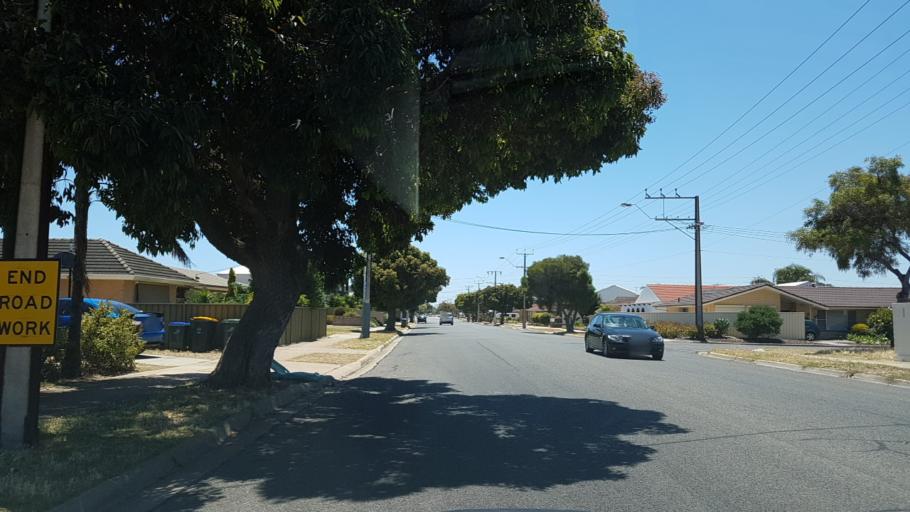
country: AU
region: South Australia
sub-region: Charles Sturt
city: West Lakes Shore
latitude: -34.8594
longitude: 138.4836
